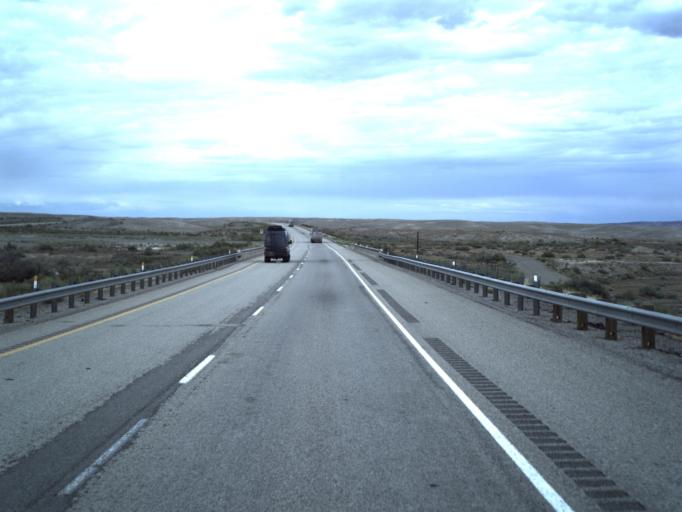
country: US
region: Utah
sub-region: Grand County
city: Moab
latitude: 38.9745
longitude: -109.3529
